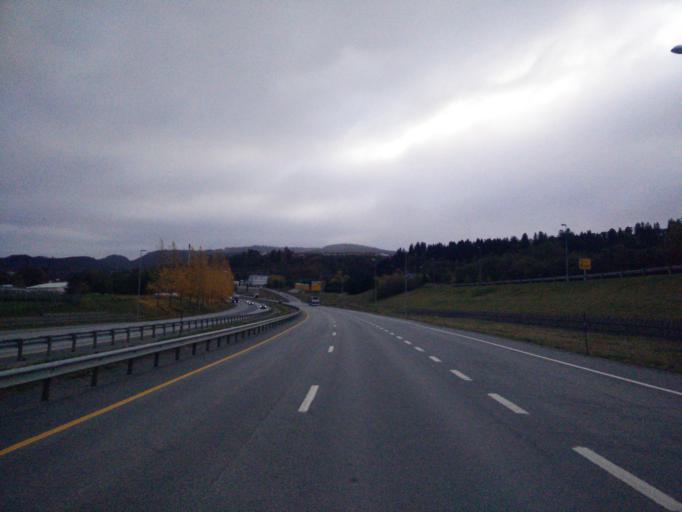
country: NO
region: Sor-Trondelag
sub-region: Trondheim
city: Trondheim
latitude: 63.4234
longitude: 10.5221
